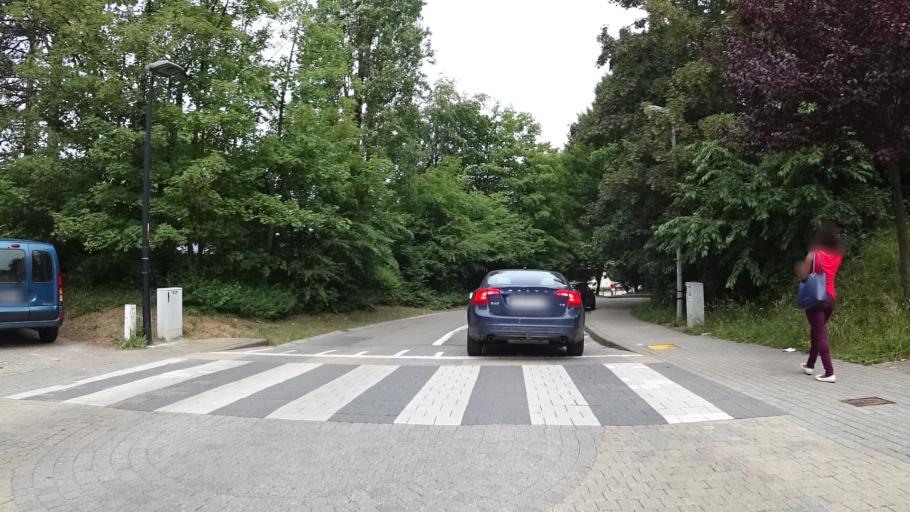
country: BE
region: Wallonia
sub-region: Province du Brabant Wallon
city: Louvain-la-Neuve
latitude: 50.6702
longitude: 4.6197
